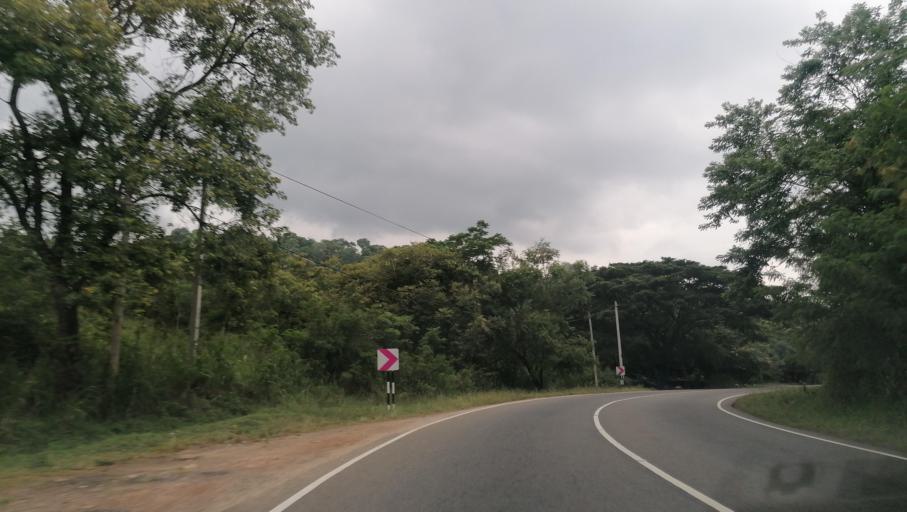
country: LK
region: Central
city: Kandy
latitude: 7.2408
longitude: 80.7275
